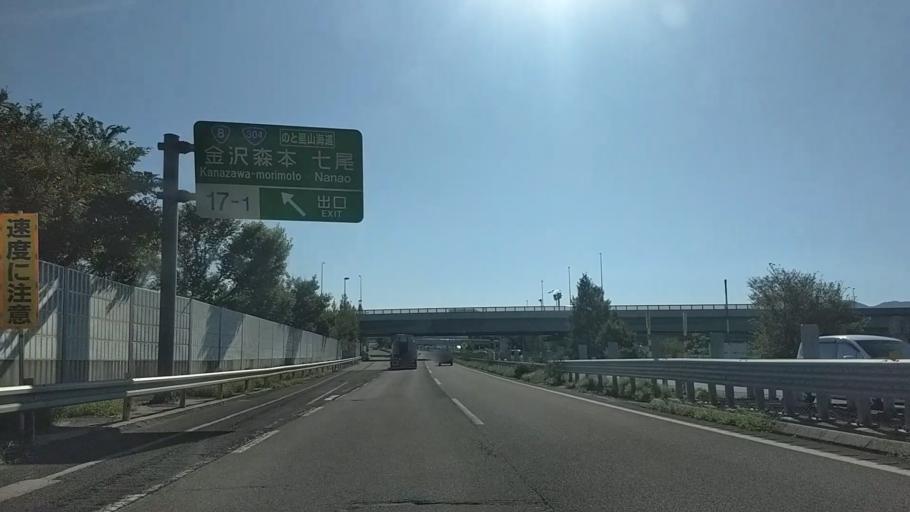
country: JP
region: Ishikawa
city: Tsubata
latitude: 36.6080
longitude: 136.7020
